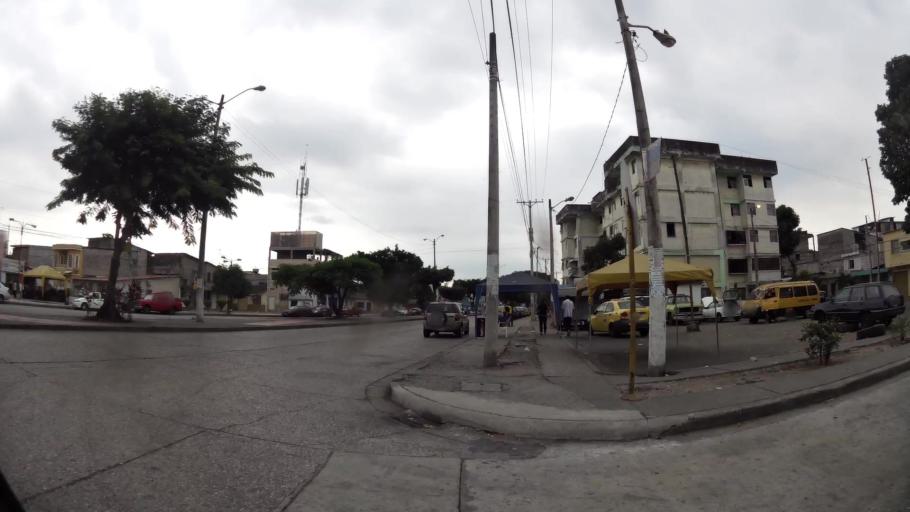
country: EC
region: Guayas
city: Eloy Alfaro
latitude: -2.1224
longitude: -79.8899
